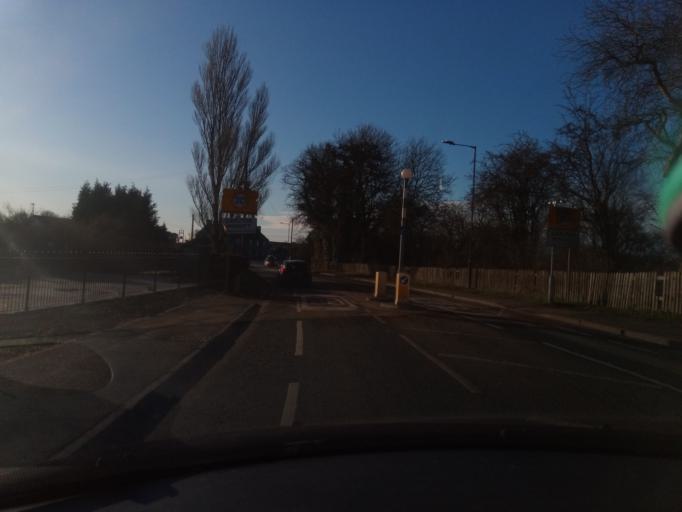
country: GB
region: England
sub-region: North Yorkshire
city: Thirsk
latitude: 54.2282
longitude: -1.3688
